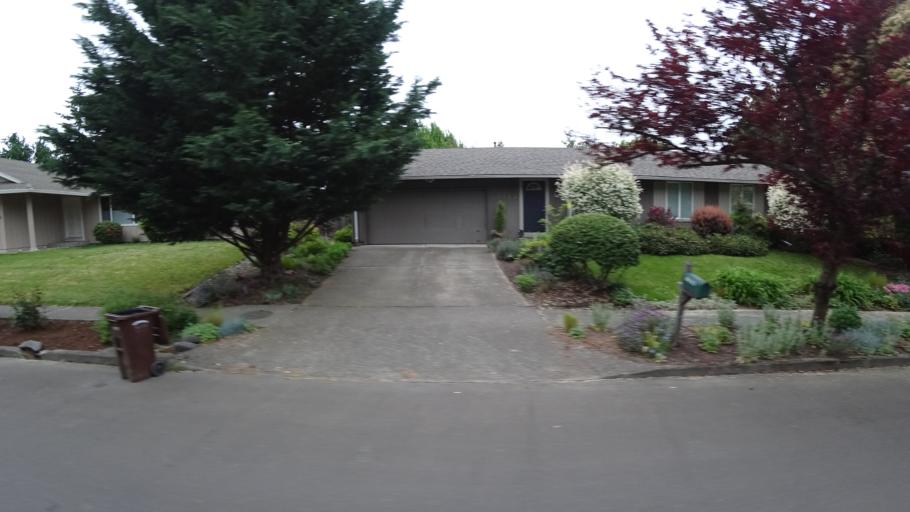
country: US
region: Oregon
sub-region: Washington County
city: Bethany
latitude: 45.5418
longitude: -122.8621
